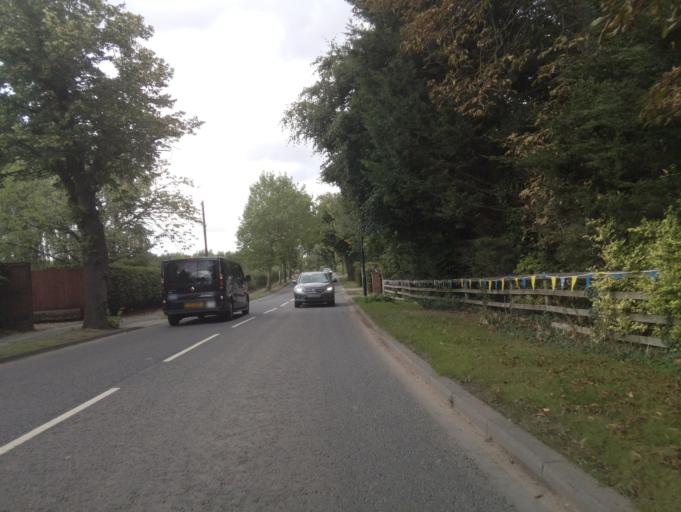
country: GB
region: England
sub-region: North Yorkshire
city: Ripon
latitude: 54.1475
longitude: -1.5305
